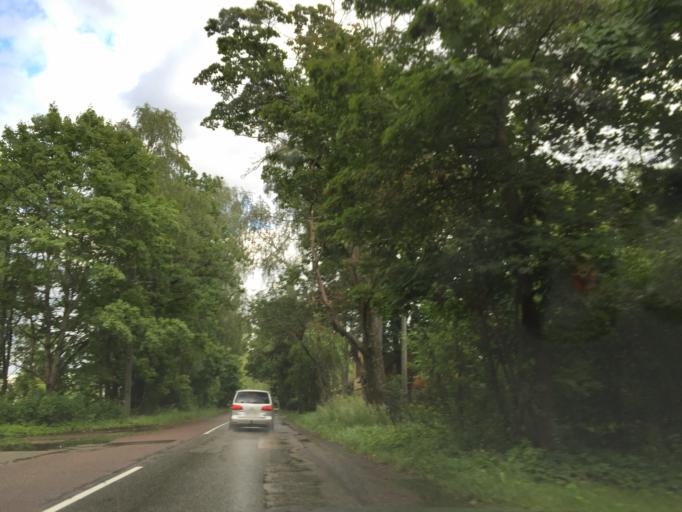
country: LV
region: Babite
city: Pinki
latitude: 56.9538
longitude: 23.9745
